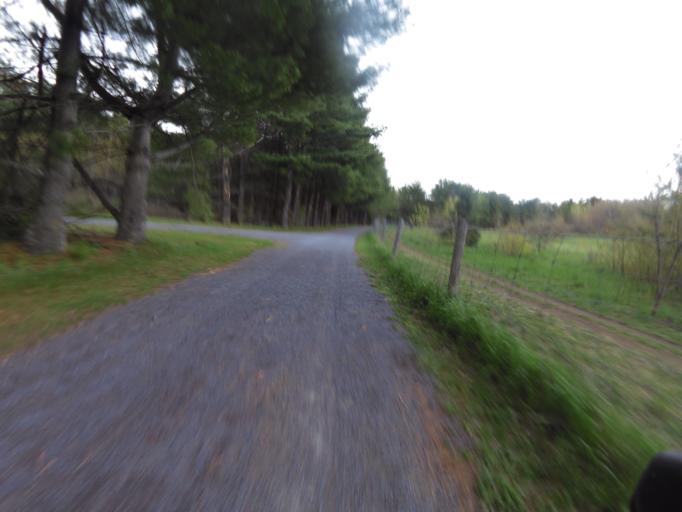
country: CA
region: Ontario
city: Bells Corners
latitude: 45.3269
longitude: -75.7964
